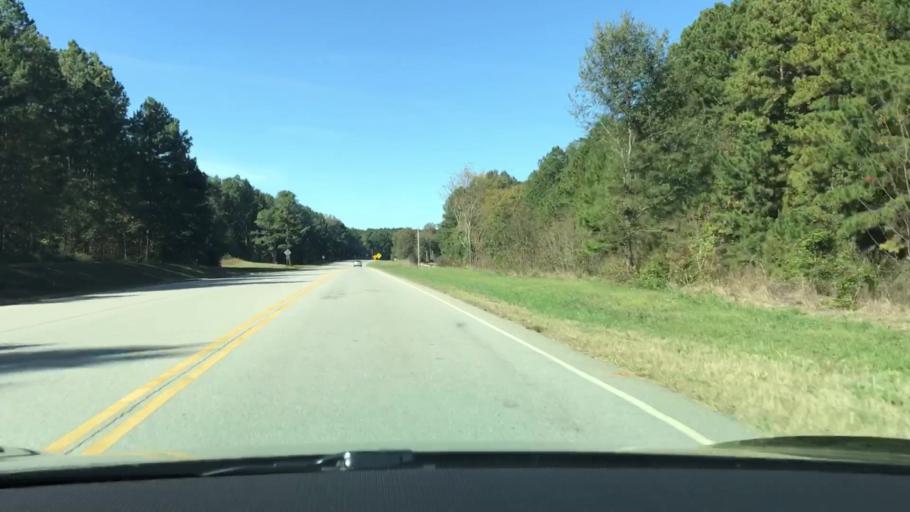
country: US
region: Georgia
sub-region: Warren County
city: Firing Range
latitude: 33.4833
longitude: -82.7858
